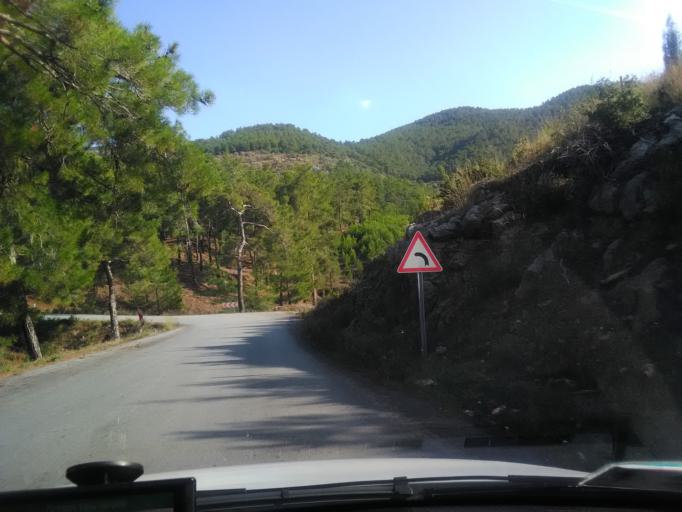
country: TR
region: Antalya
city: Gazipasa
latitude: 36.3000
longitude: 32.3412
